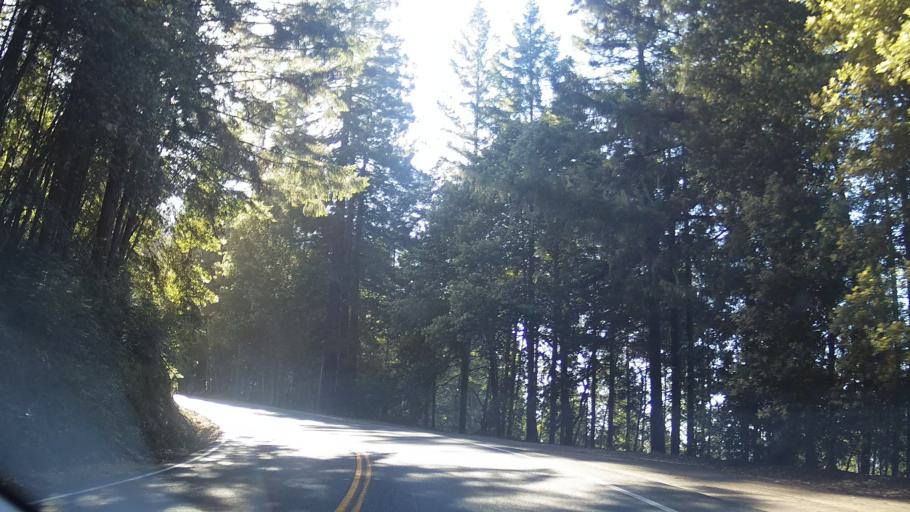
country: US
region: California
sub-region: Mendocino County
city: Brooktrails
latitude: 39.3930
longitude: -123.4625
